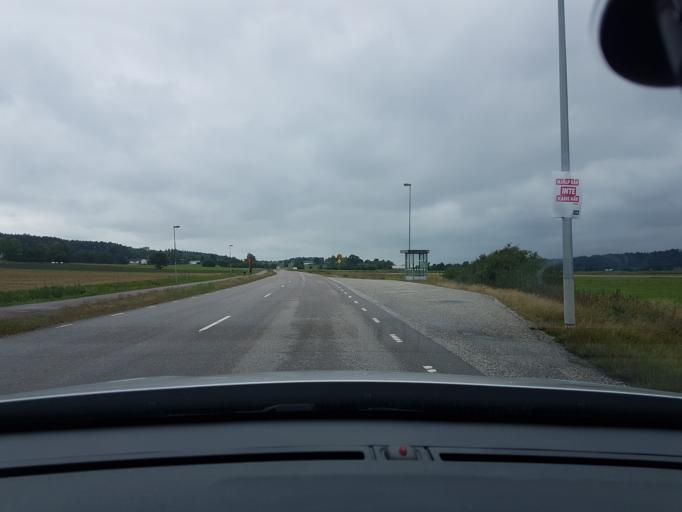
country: SE
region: Vaestra Goetaland
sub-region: Ale Kommun
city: Skepplanda
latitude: 57.9758
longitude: 12.1856
